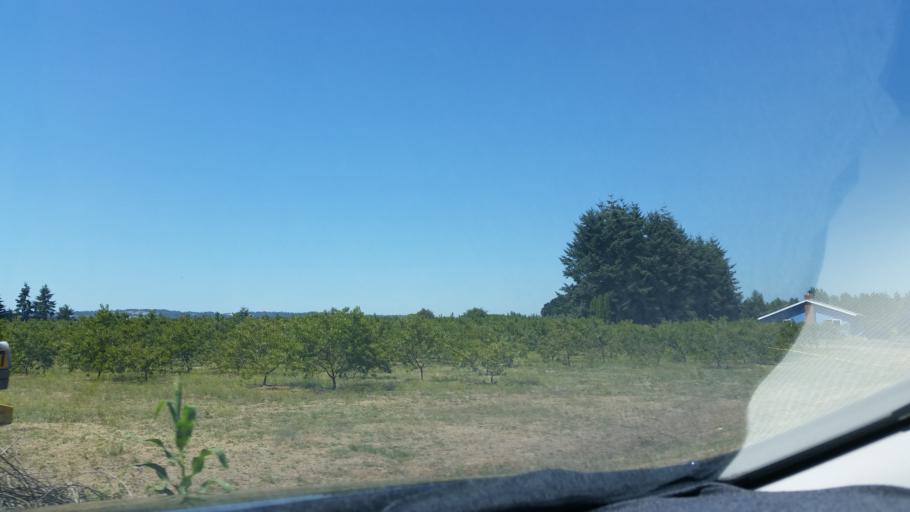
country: US
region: Oregon
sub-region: Clackamas County
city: Wilsonville
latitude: 45.2596
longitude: -122.7821
